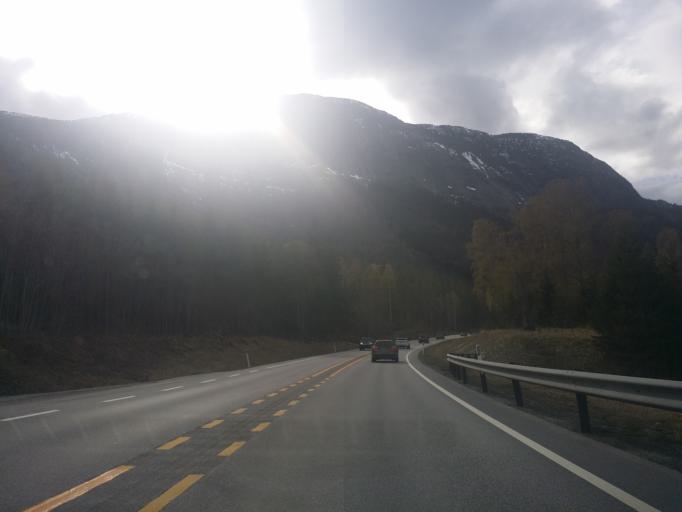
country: NO
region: Buskerud
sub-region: Fla
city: Fla
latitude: 60.4441
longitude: 9.2943
